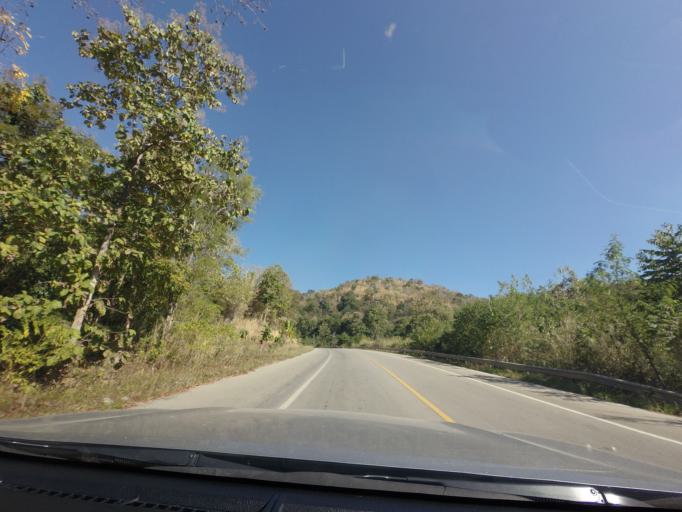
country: TH
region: Lampang
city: Mae Mo
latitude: 18.4845
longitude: 99.6394
